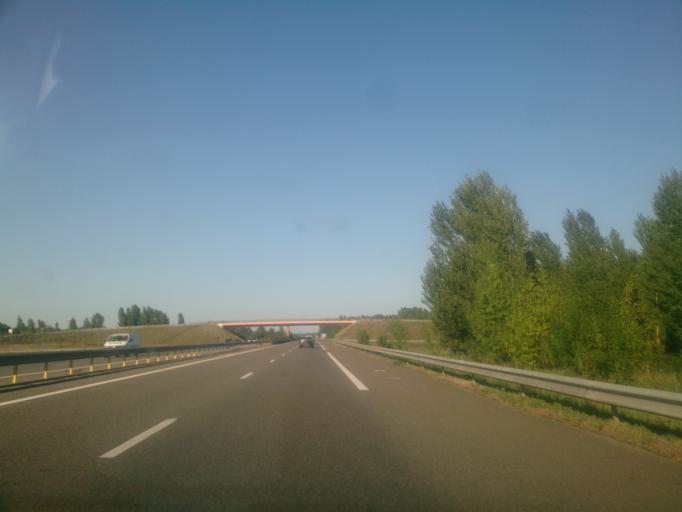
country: FR
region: Midi-Pyrenees
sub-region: Departement du Tarn-et-Garonne
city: Realville
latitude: 44.1354
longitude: 1.4913
